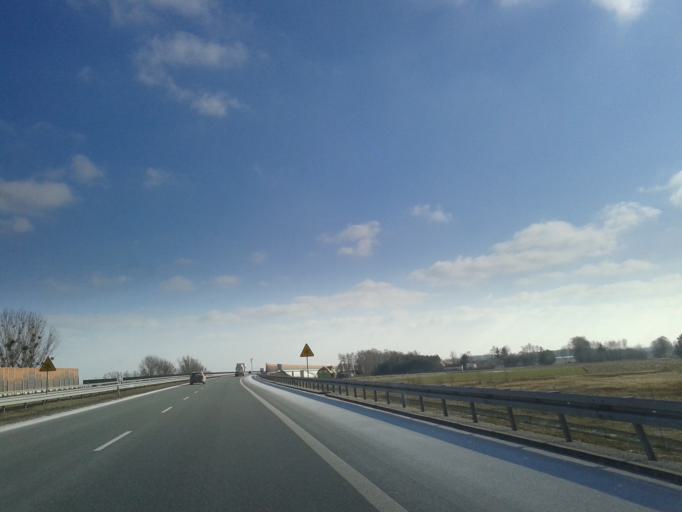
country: PL
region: Kujawsko-Pomorskie
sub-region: Powiat aleksandrowski
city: Waganiec
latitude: 52.7963
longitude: 18.8325
